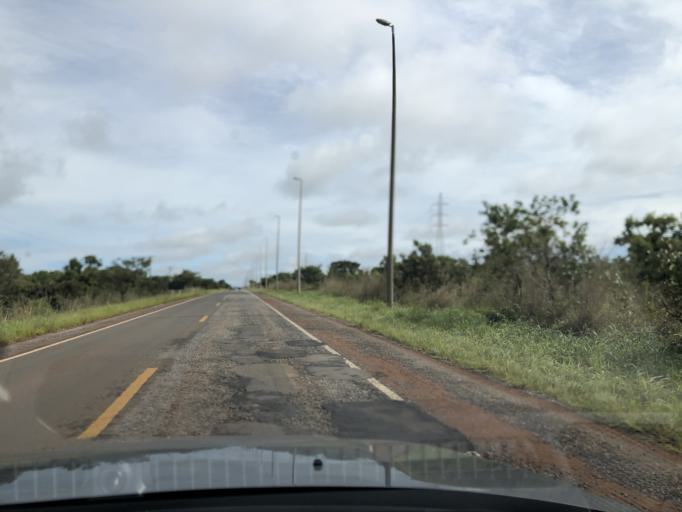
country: BR
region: Federal District
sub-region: Brasilia
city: Brasilia
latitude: -15.7035
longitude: -48.0880
